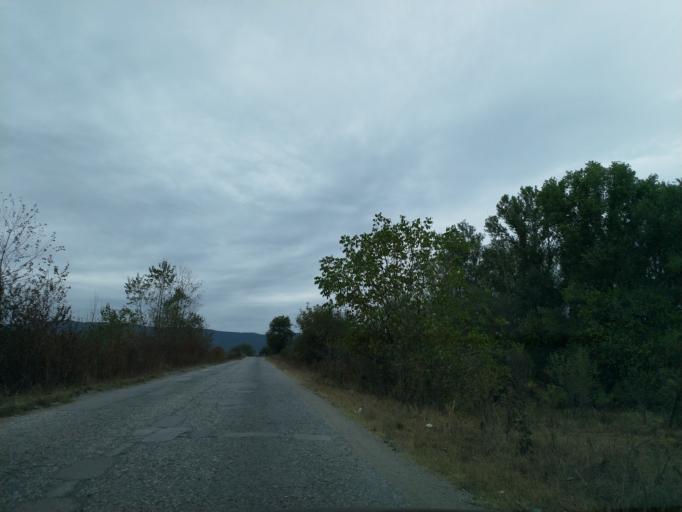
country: RS
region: Central Serbia
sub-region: Pomoravski Okrug
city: Paracin
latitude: 43.8273
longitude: 21.3485
